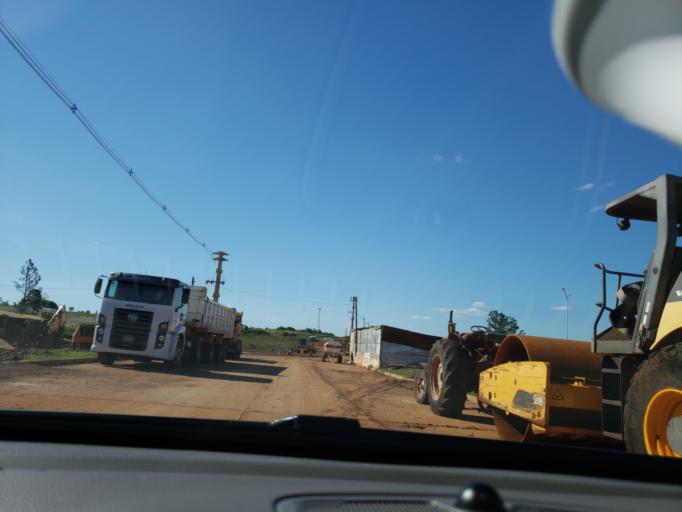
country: AR
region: Misiones
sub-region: Departamento de Capital
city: Posadas
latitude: -27.3985
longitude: -55.9898
